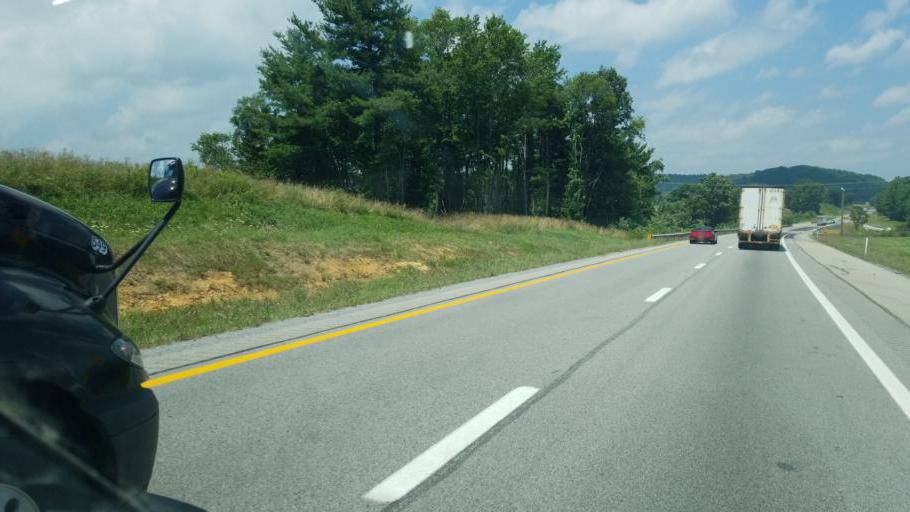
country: US
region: West Virginia
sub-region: Mercer County
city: Athens
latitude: 37.4232
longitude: -81.0658
